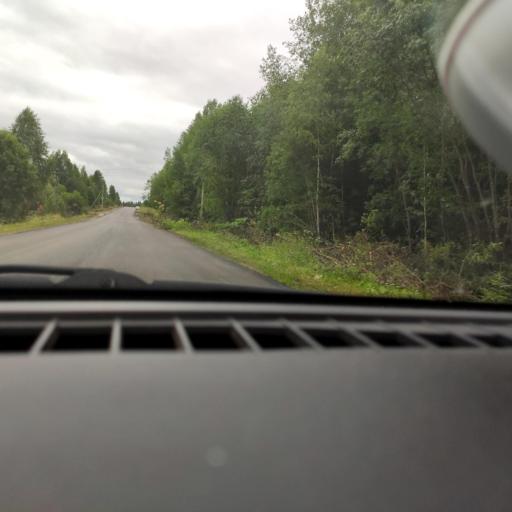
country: RU
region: Perm
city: Polazna
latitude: 58.3356
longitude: 56.2049
